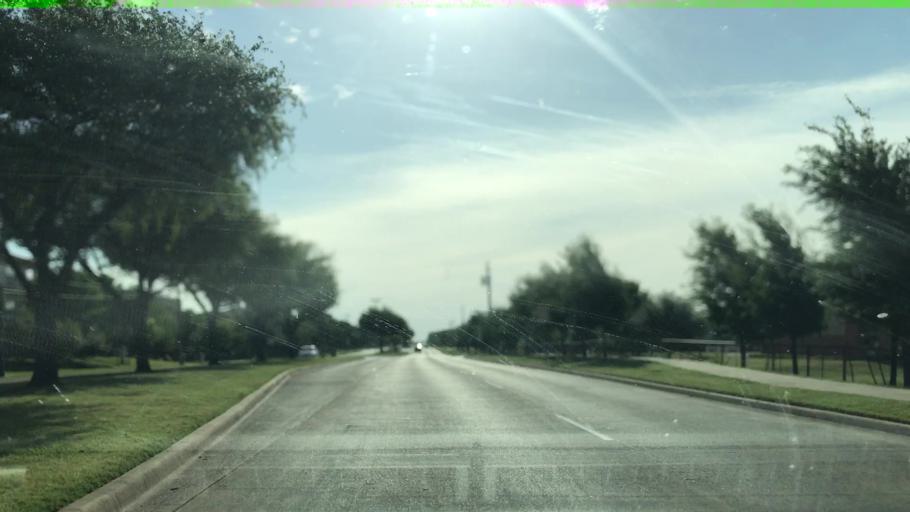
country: US
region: Texas
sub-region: Dallas County
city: Farmers Branch
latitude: 32.8957
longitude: -96.9368
